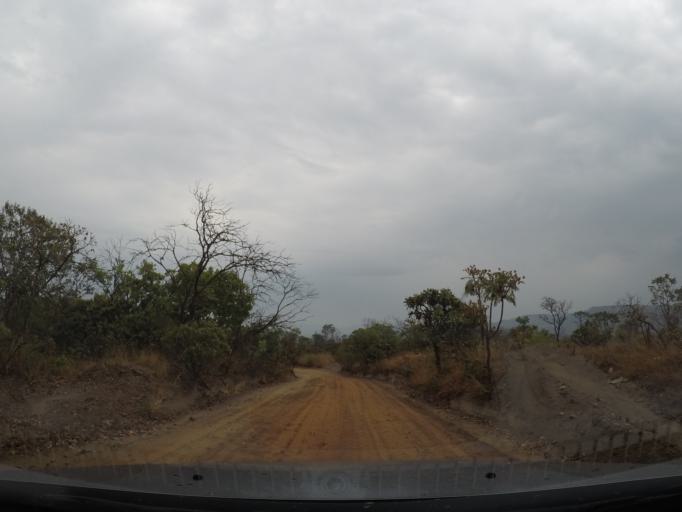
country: BR
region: Goias
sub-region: Pirenopolis
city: Pirenopolis
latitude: -15.8312
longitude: -48.9099
